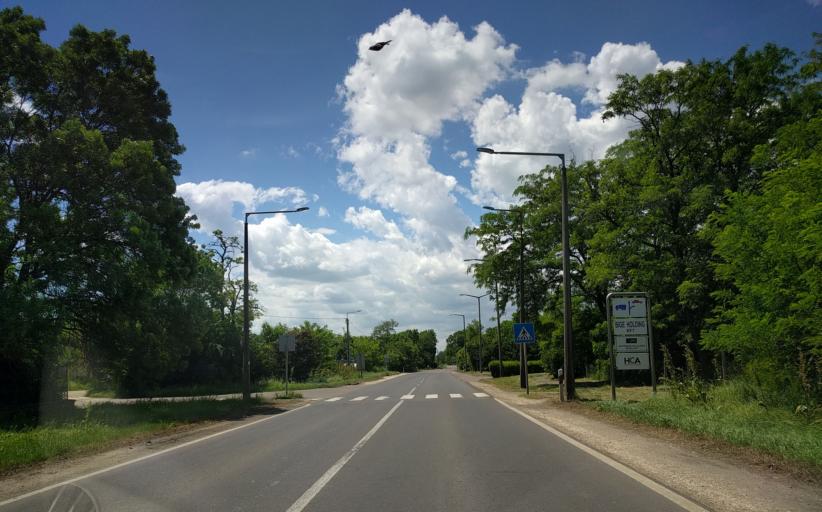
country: HU
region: Jasz-Nagykun-Szolnok
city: Toszeg
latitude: 47.1356
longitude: 20.1490
